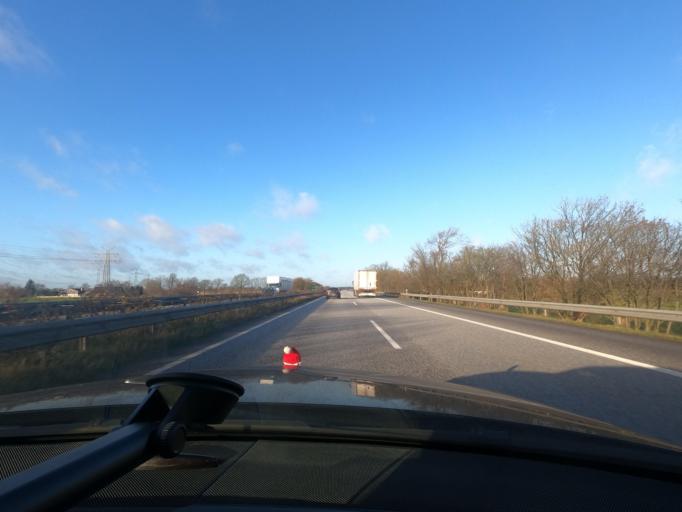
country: DE
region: Schleswig-Holstein
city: Oeversee
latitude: 54.6860
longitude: 9.4143
